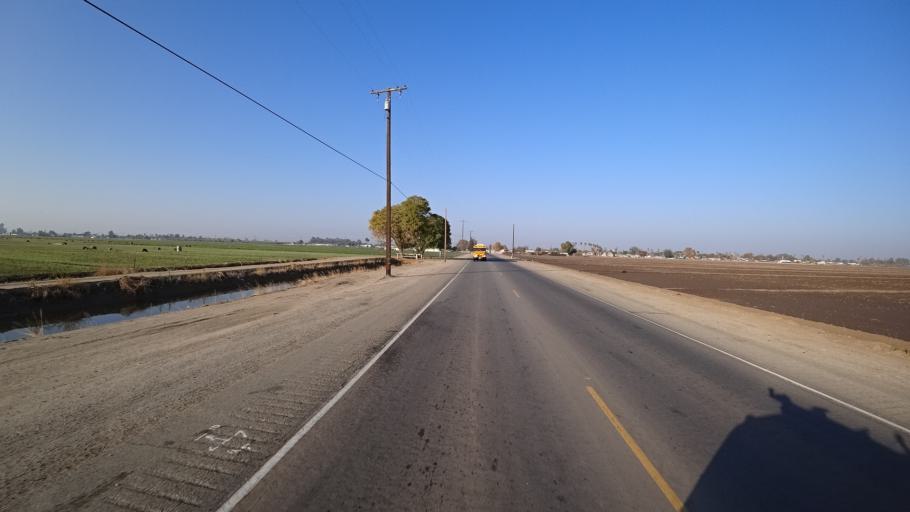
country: US
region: California
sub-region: Kern County
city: Greenfield
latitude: 35.2668
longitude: -118.9952
